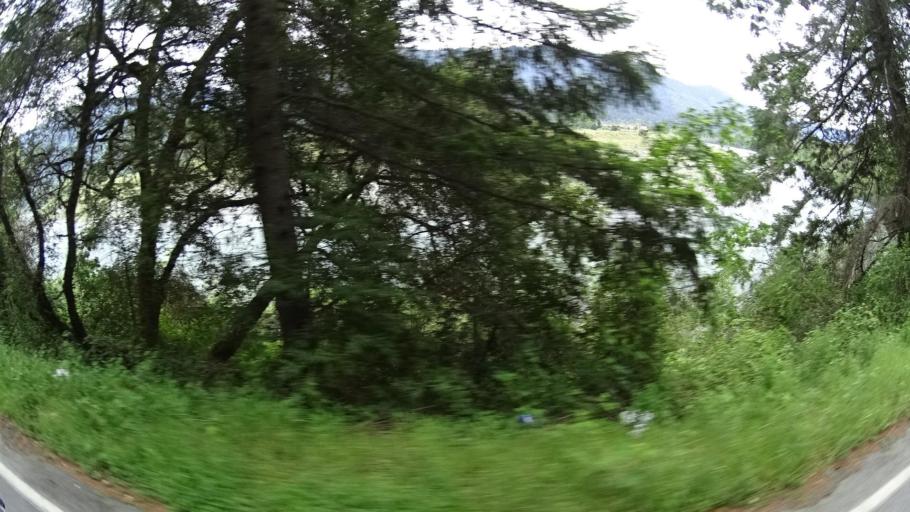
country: US
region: California
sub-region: Humboldt County
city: Willow Creek
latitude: 41.0647
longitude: -123.6951
